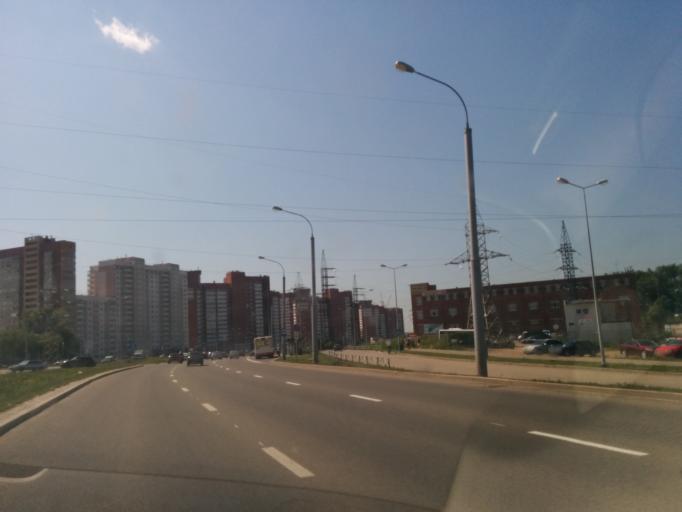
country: RU
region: Perm
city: Perm
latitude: 57.9888
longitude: 56.2946
